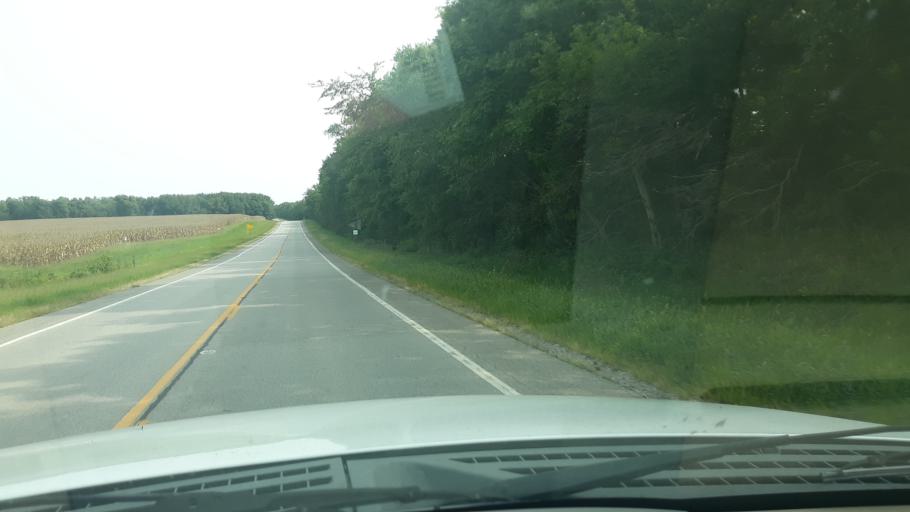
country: US
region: Illinois
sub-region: Edwards County
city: Grayville
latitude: 38.1742
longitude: -88.0531
